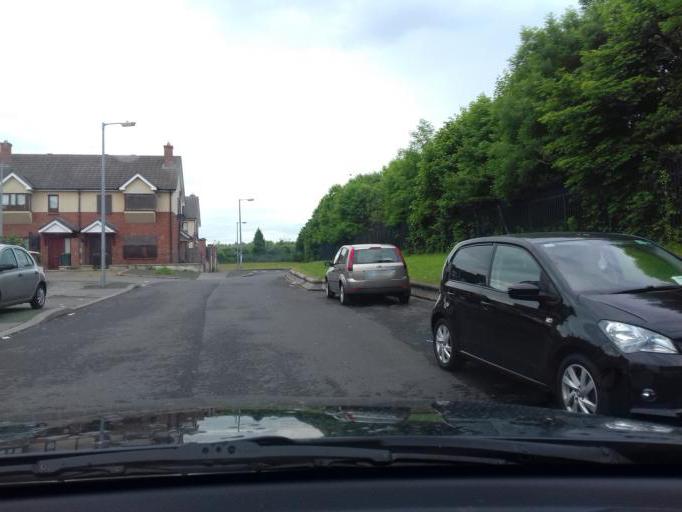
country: IE
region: Leinster
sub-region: Fingal County
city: Blanchardstown
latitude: 53.4052
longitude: -6.3866
